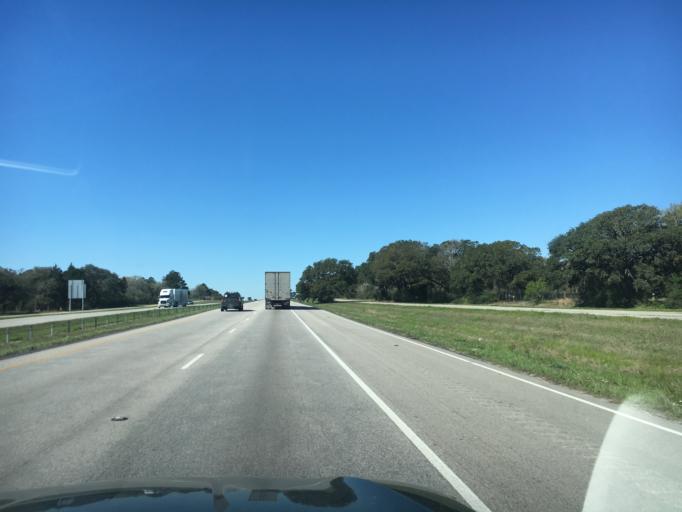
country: US
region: Texas
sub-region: Colorado County
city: Columbus
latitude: 29.7209
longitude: -96.4329
